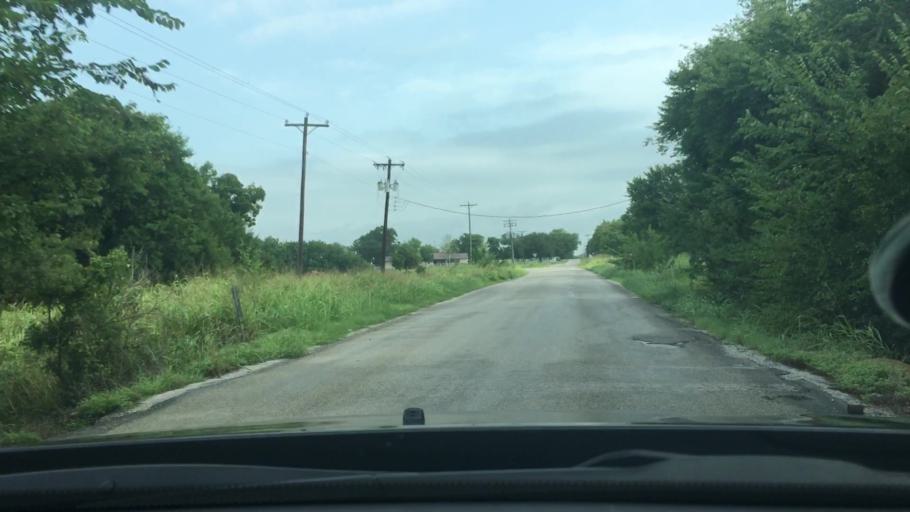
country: US
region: Oklahoma
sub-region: Carter County
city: Lone Grove
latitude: 34.2142
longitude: -97.2650
